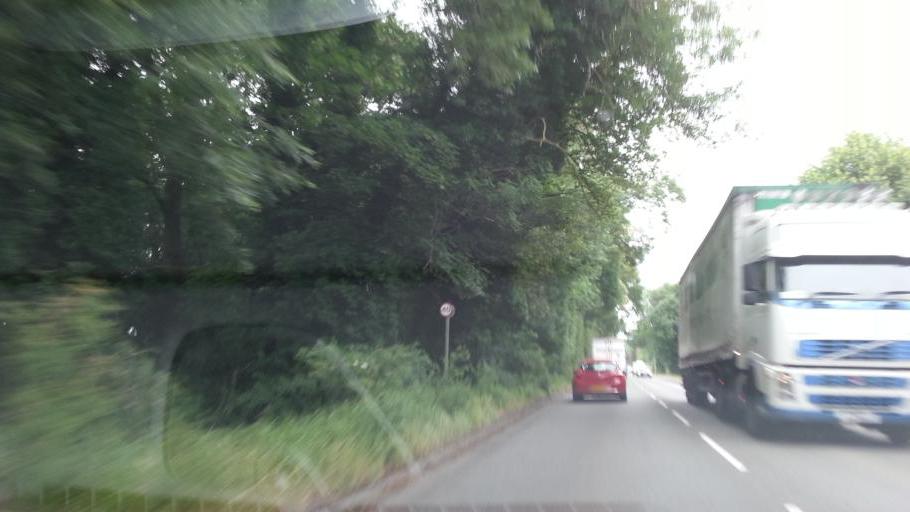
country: GB
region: England
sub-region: Northamptonshire
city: Northampton
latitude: 52.2817
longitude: -0.8440
